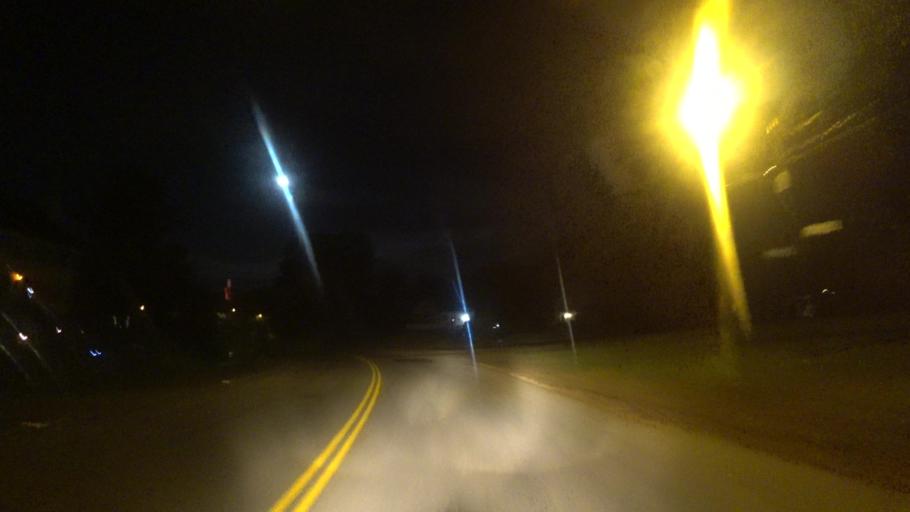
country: US
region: New Hampshire
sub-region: Rockingham County
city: Plaistow
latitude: 42.8059
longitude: -71.1066
